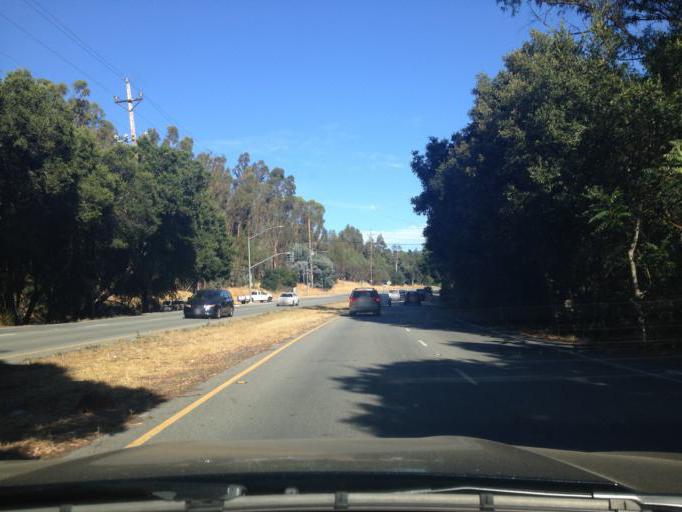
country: US
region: California
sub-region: Santa Clara County
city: Monte Sereno
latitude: 37.2405
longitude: -121.9982
